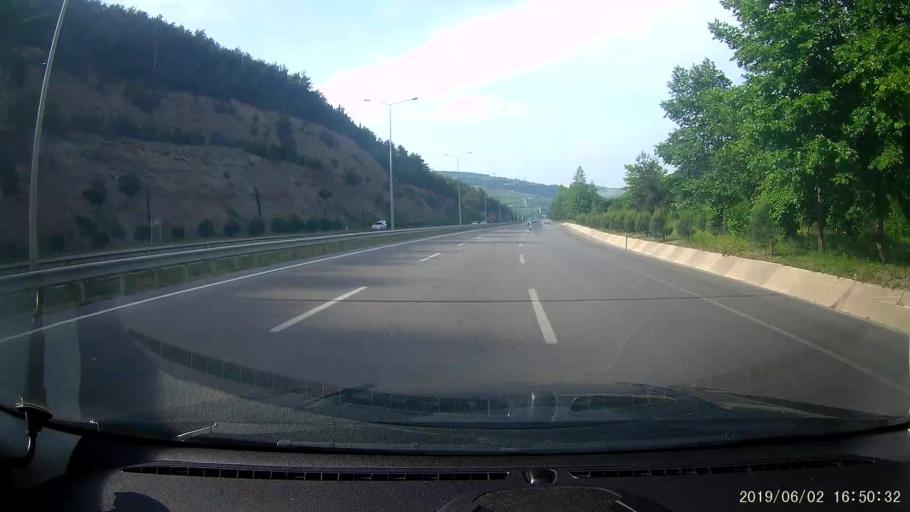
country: TR
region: Samsun
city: Samsun
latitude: 41.2565
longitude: 36.1738
